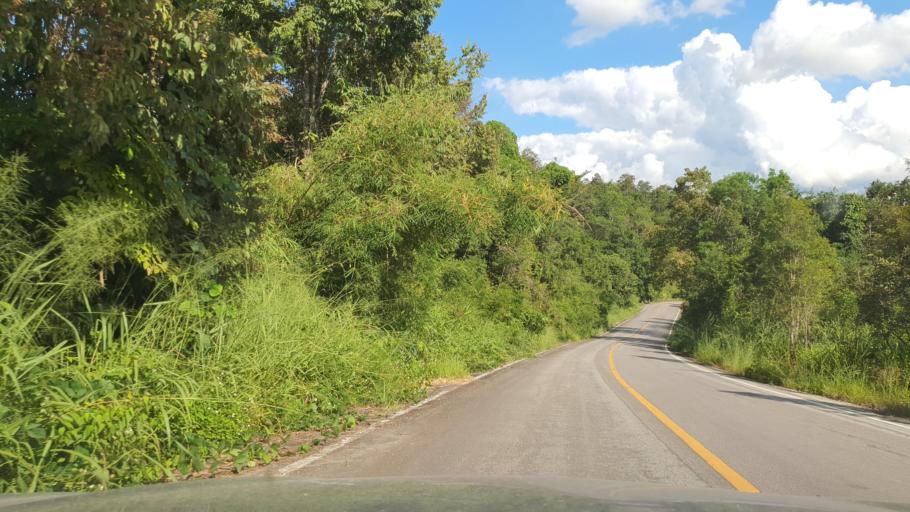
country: TH
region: Chiang Rai
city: Wiang Pa Pao
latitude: 19.3331
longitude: 99.4575
